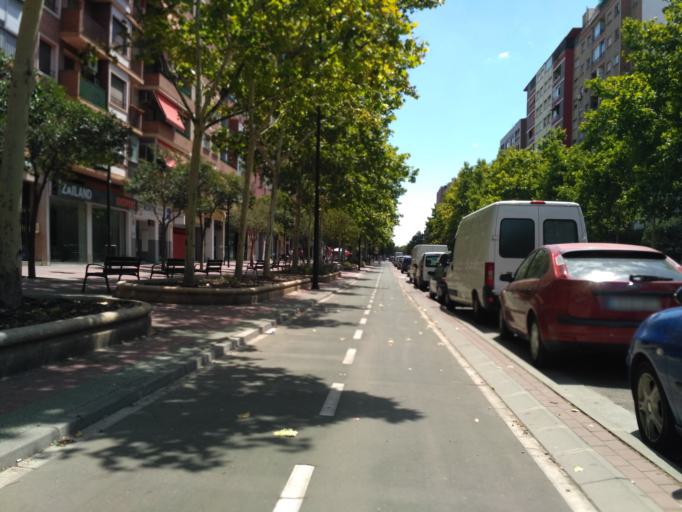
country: ES
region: Aragon
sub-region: Provincia de Zaragoza
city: Delicias
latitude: 41.6521
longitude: -0.9036
